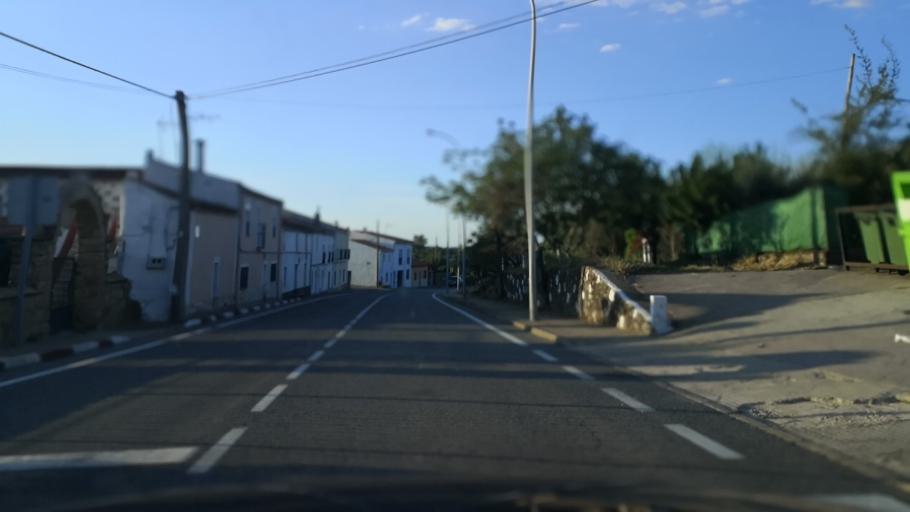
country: PT
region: Portalegre
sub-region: Portalegre
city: Sao Juliao
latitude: 39.3506
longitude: -7.2748
